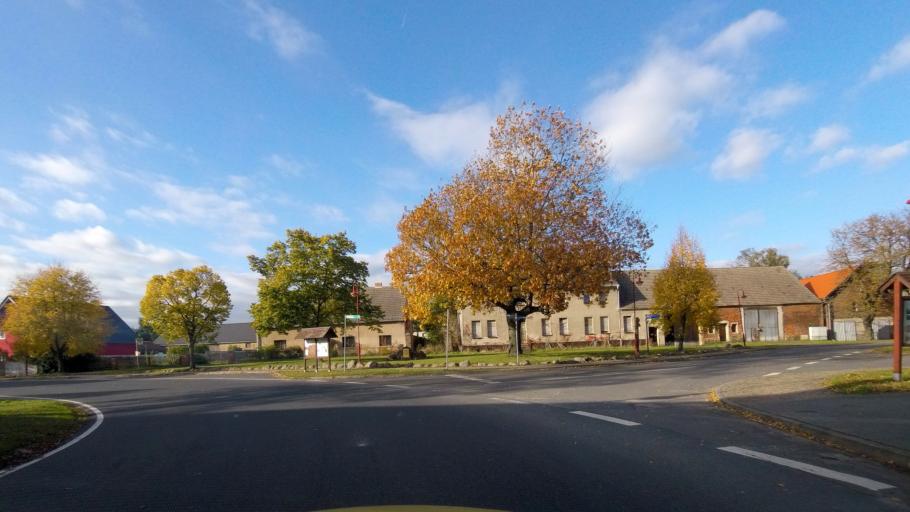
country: DE
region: Saxony-Anhalt
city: Seyda
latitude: 51.9518
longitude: 12.9124
